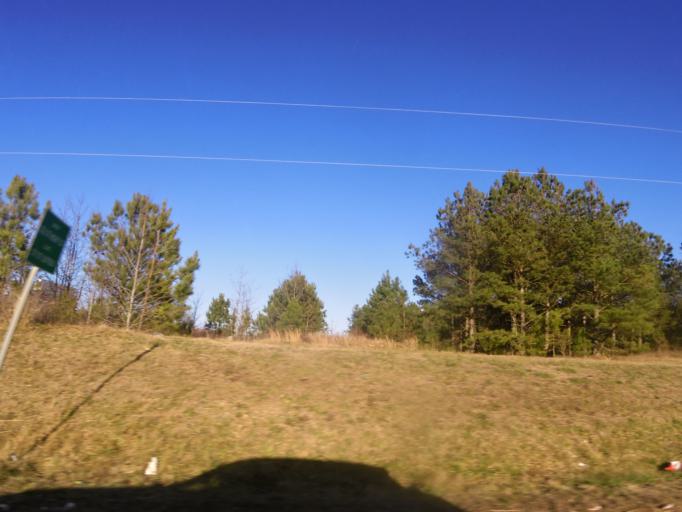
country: US
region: Virginia
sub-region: City of Franklin
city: Franklin
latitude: 36.6591
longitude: -76.8789
